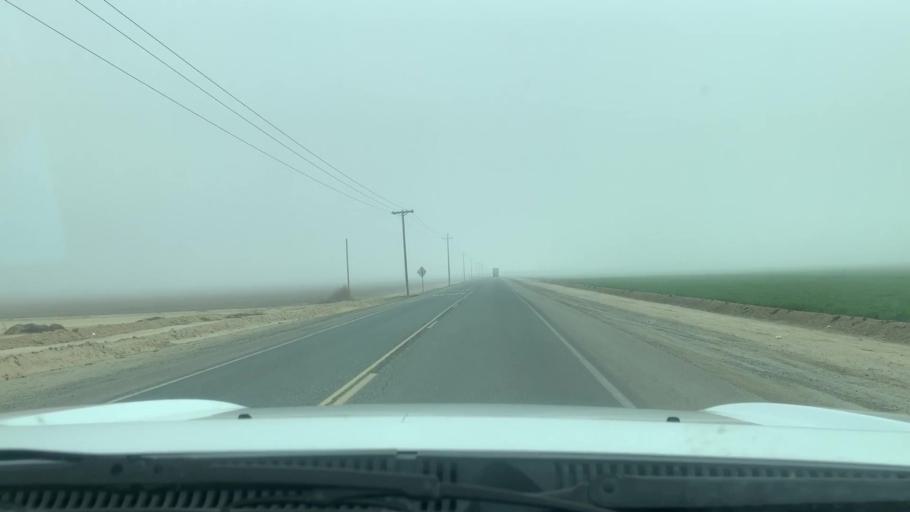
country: US
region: California
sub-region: Kern County
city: Buttonwillow
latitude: 35.5005
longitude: -119.4727
